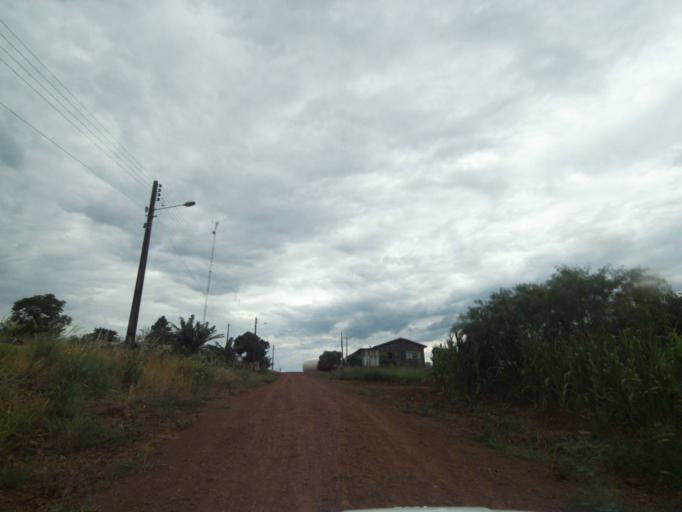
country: BR
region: Parana
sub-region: Guaraniacu
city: Guaraniacu
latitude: -24.9223
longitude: -52.9388
